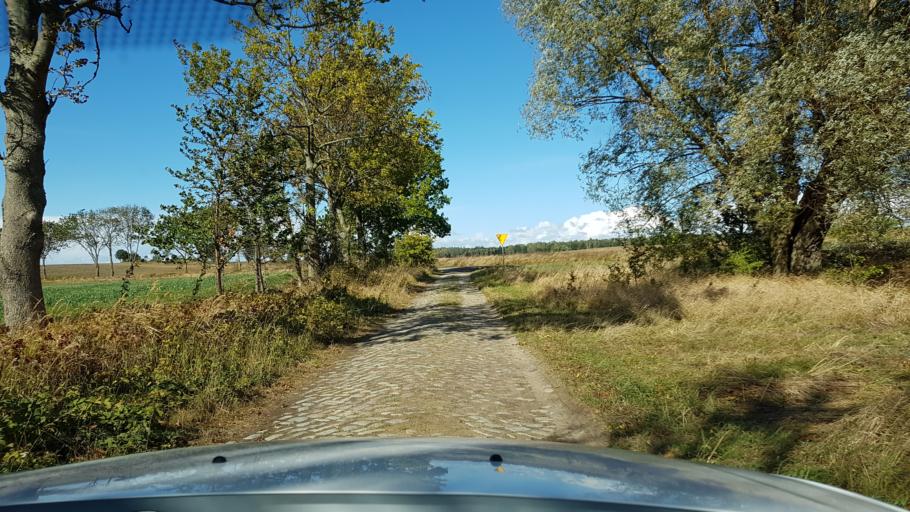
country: PL
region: West Pomeranian Voivodeship
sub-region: Powiat gryfinski
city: Banie
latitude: 53.1416
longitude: 14.6426
